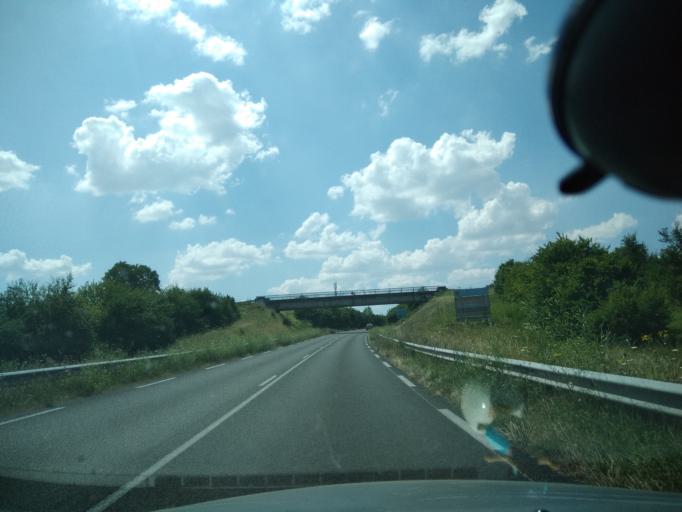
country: FR
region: Centre
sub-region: Departement d'Indre-et-Loire
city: Blere
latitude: 47.3150
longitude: 0.9966
